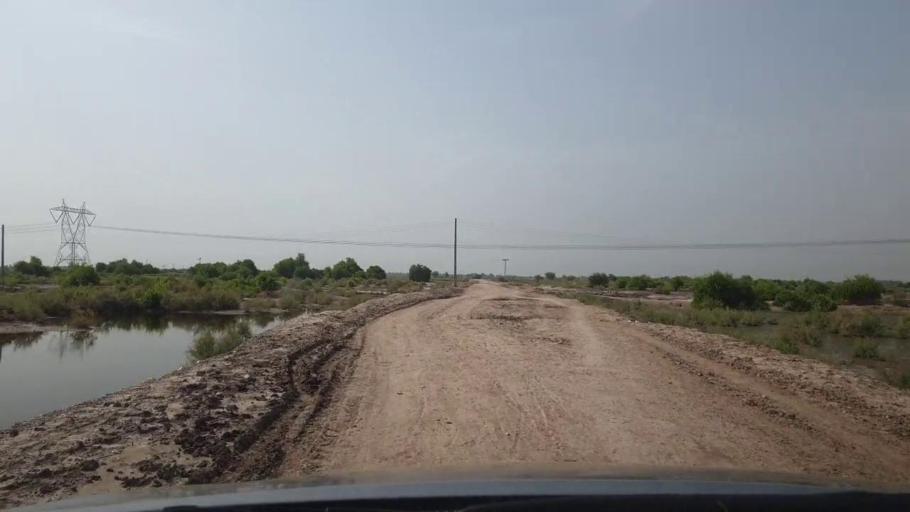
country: PK
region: Sindh
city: Rohri
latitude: 27.6763
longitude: 69.0121
